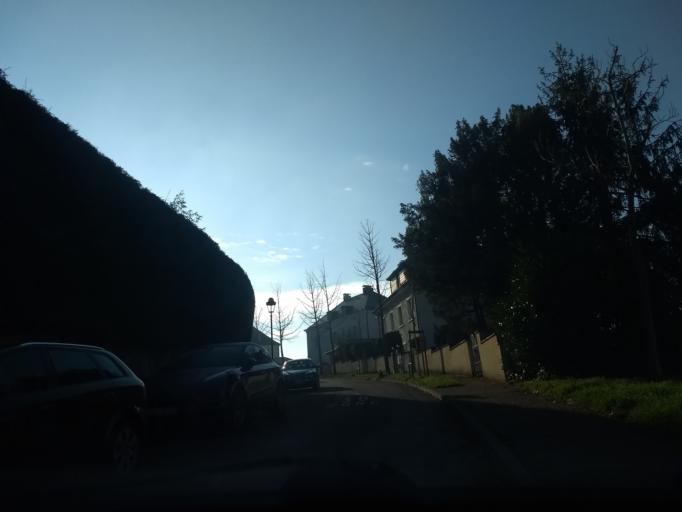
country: DE
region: Baden-Wuerttemberg
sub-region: Karlsruhe Region
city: Baden-Baden
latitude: 48.7633
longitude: 8.2502
